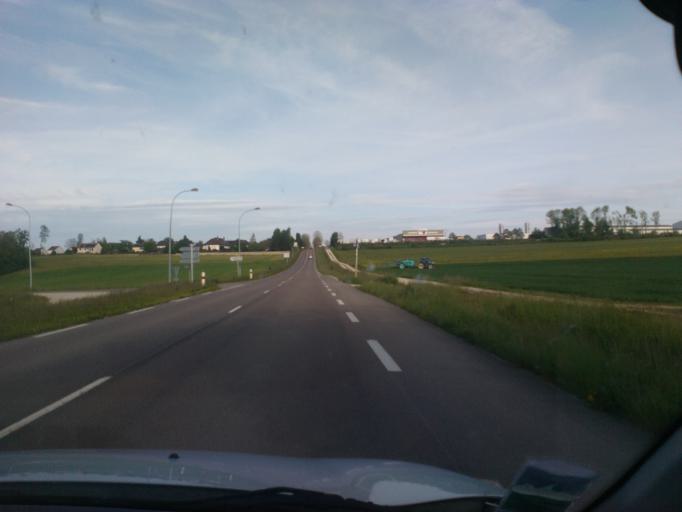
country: FR
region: Champagne-Ardenne
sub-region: Departement de l'Aube
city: Vendeuvre-sur-Barse
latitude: 48.2383
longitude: 4.4876
